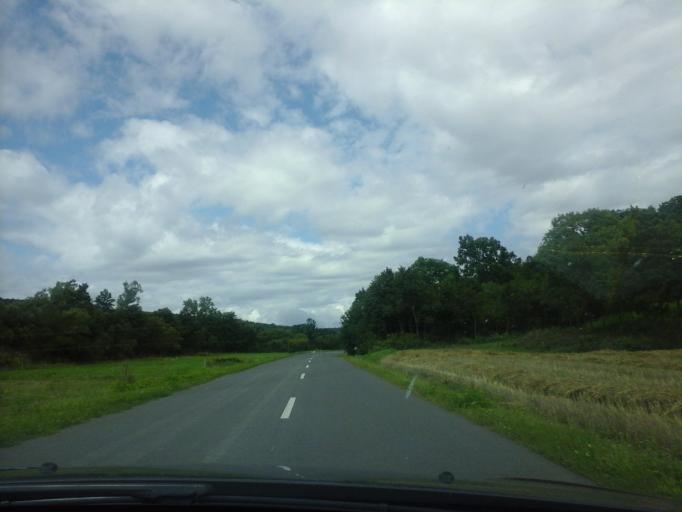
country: HU
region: Borsod-Abauj-Zemplen
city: Rudabanya
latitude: 48.4139
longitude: 20.5077
